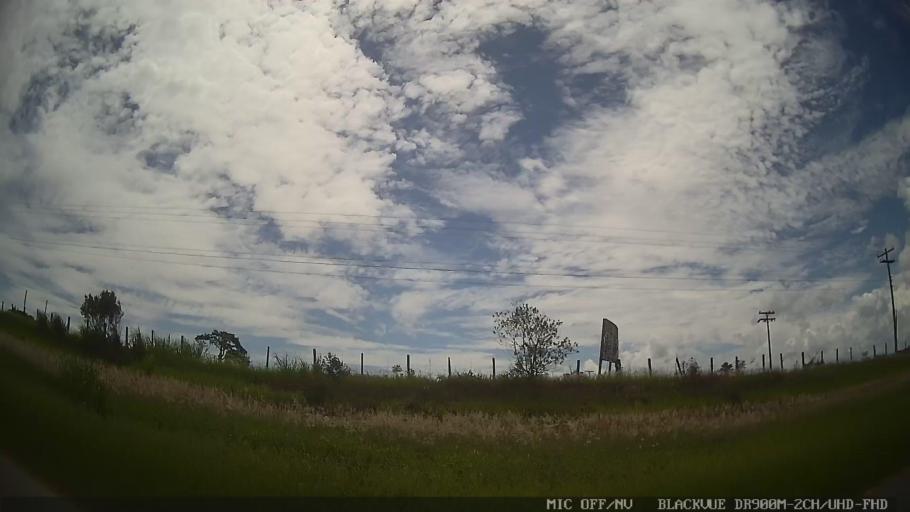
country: BR
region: Sao Paulo
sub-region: Conchas
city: Conchas
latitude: -23.0597
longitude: -47.9660
